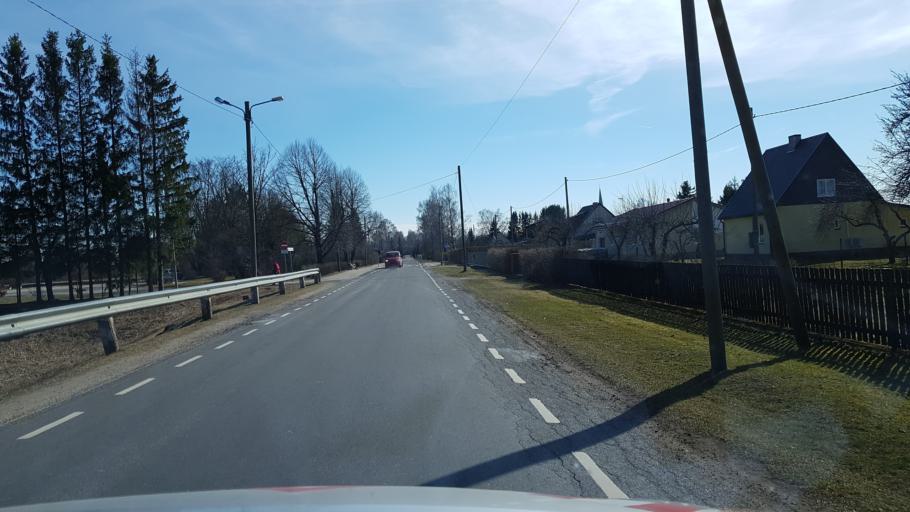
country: EE
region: Harju
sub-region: Nissi vald
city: Riisipere
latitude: 59.1093
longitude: 24.3140
